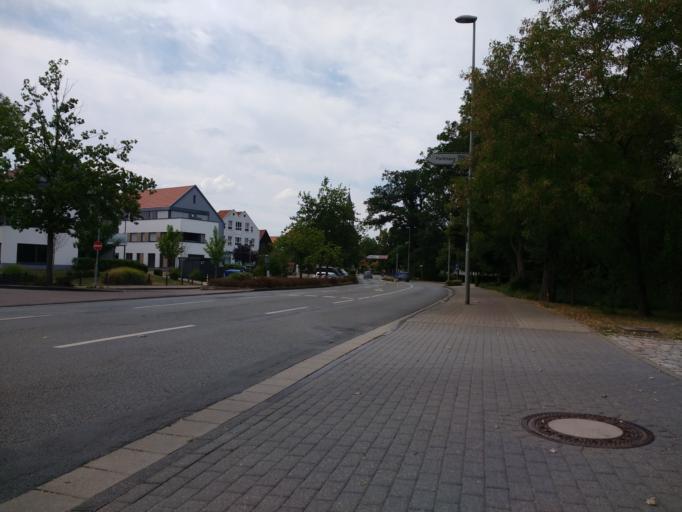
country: DE
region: Lower Saxony
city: Gifhorn
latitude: 52.4872
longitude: 10.5490
